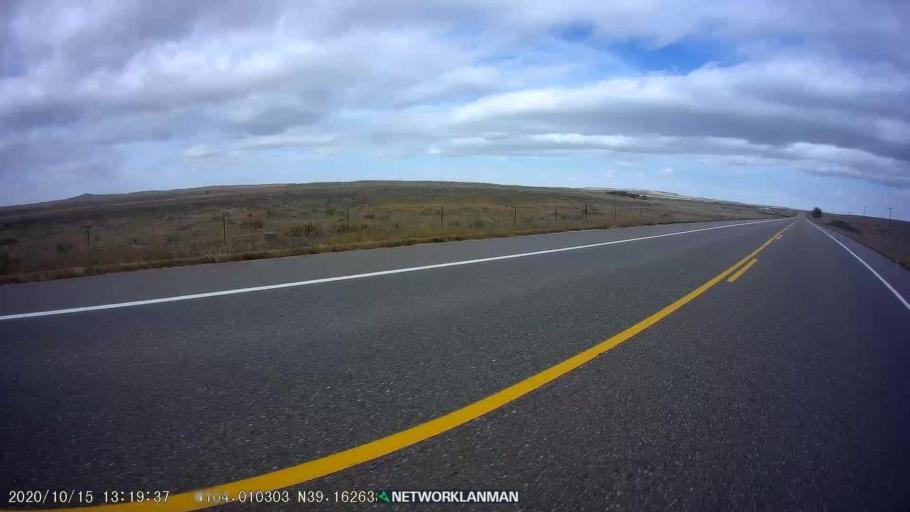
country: US
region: Colorado
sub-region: Lincoln County
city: Limon
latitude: 39.1627
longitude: -104.0099
